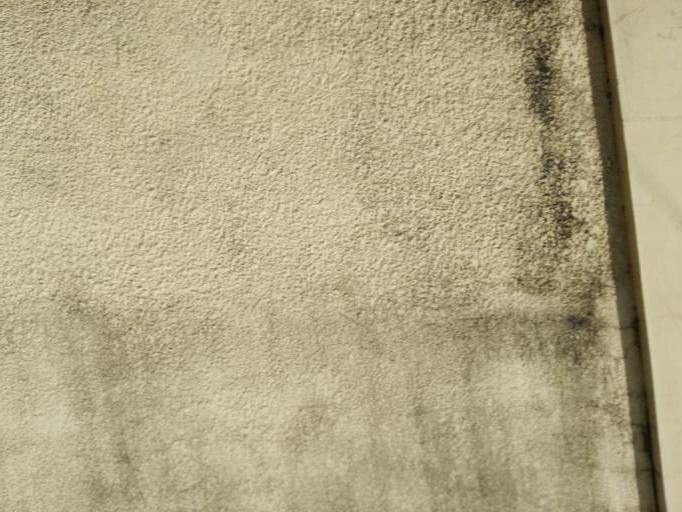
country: MU
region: Black River
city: Petite Riviere
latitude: -20.2212
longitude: 57.4621
